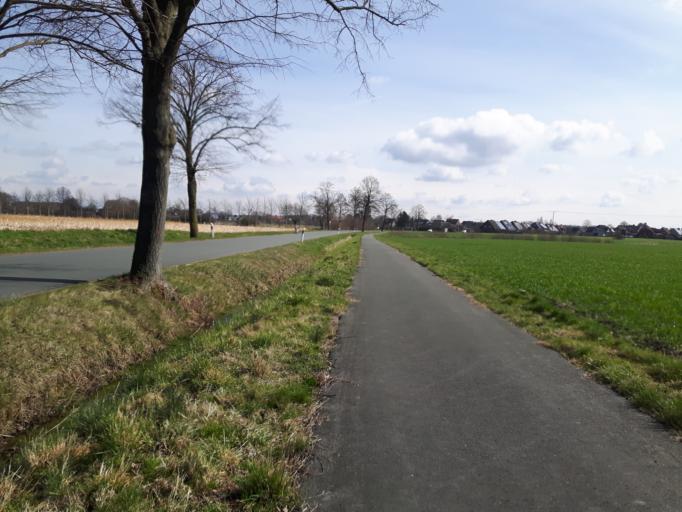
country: DE
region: North Rhine-Westphalia
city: Ludinghausen
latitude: 51.8348
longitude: 7.3900
